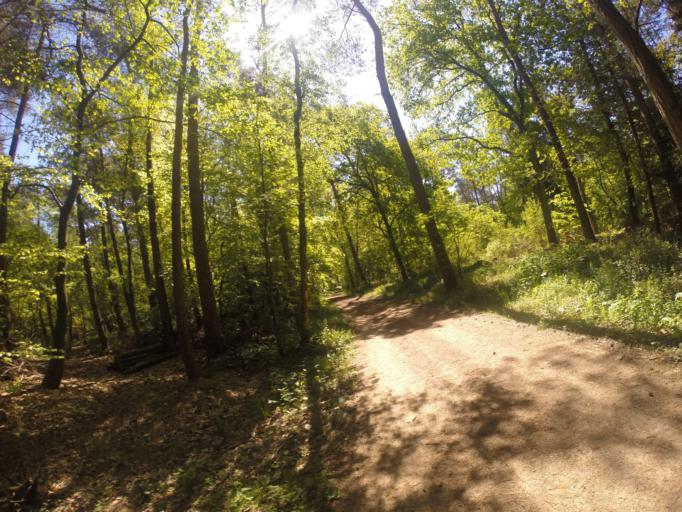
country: NL
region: Gelderland
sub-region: Gemeente Montferland
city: s-Heerenberg
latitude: 51.9123
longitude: 6.2433
